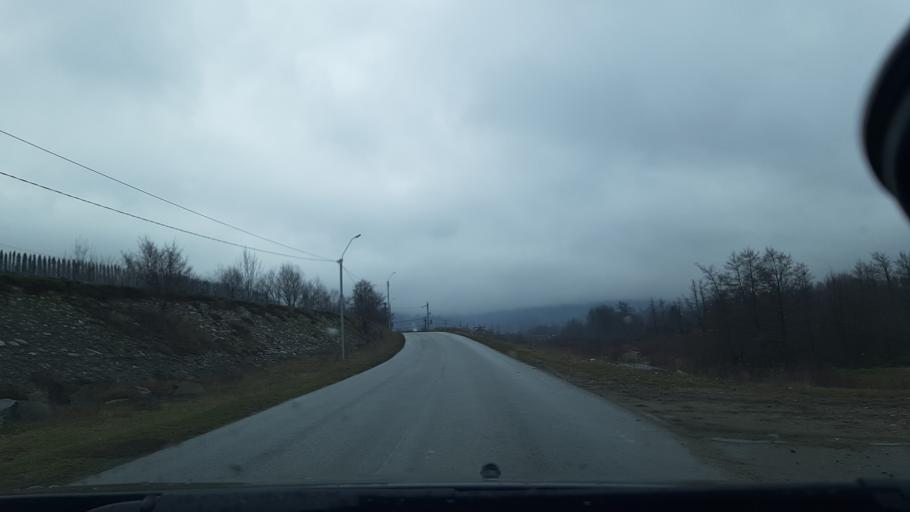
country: RO
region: Hunedoara
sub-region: Oras Petrila
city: Petrila
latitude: 45.4355
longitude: 23.4177
